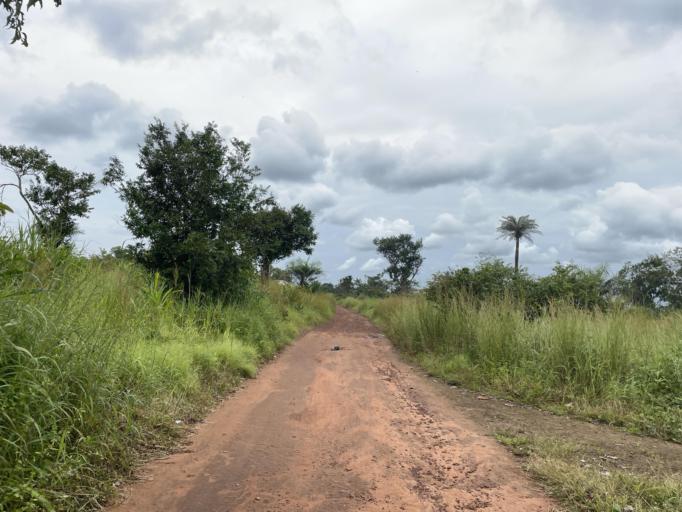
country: SL
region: Northern Province
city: Kambia
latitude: 9.1274
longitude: -12.9026
